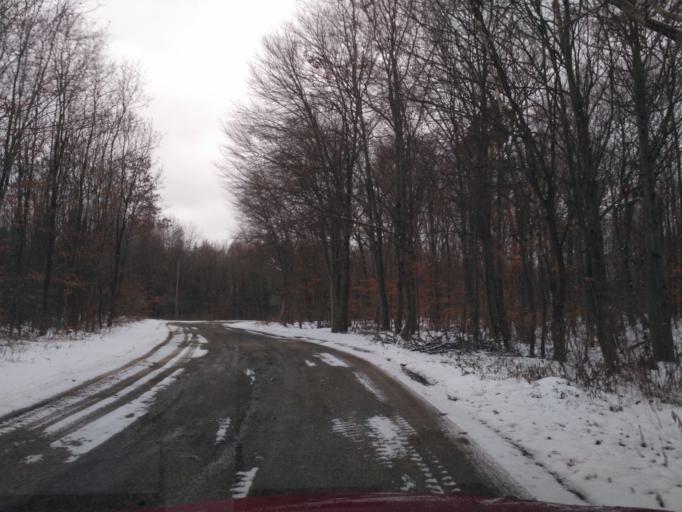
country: SK
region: Presovsky
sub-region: Okres Presov
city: Presov
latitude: 48.9919
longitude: 21.1839
